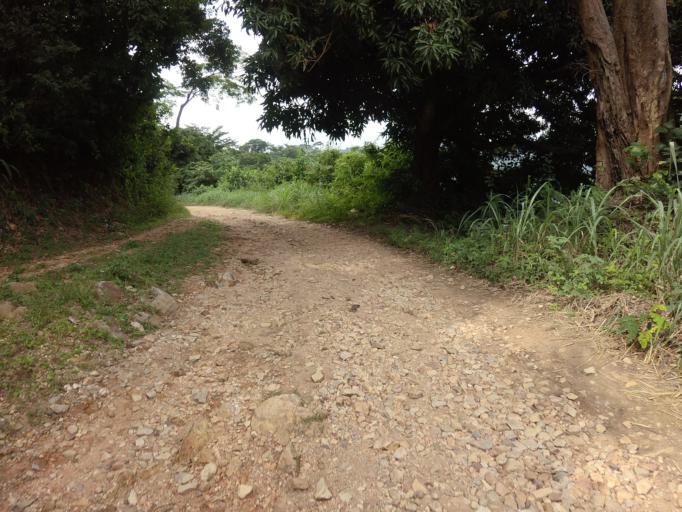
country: GH
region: Volta
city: Kpandu
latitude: 6.8696
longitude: 0.4412
